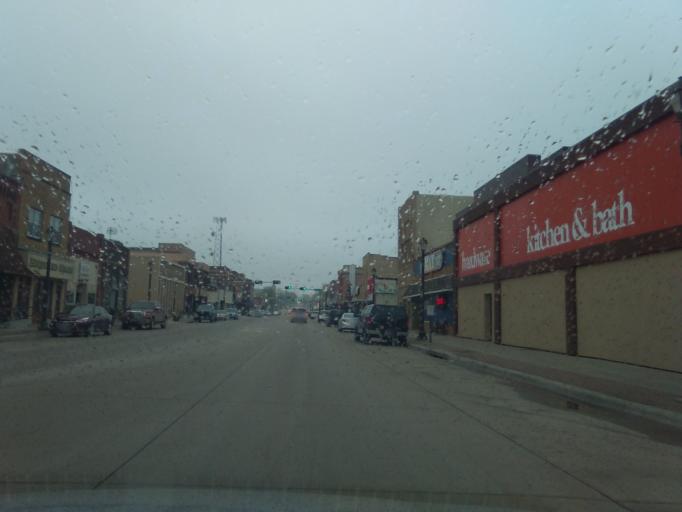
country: US
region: Nebraska
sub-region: Wayne County
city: Wayne
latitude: 42.2292
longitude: -97.0178
